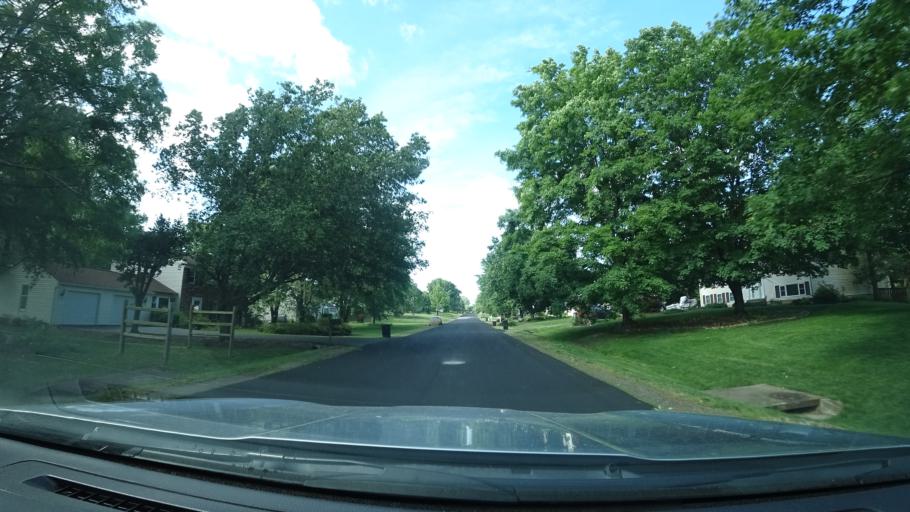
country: US
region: Virginia
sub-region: Fairfax County
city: Herndon
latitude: 38.9437
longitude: -77.3798
